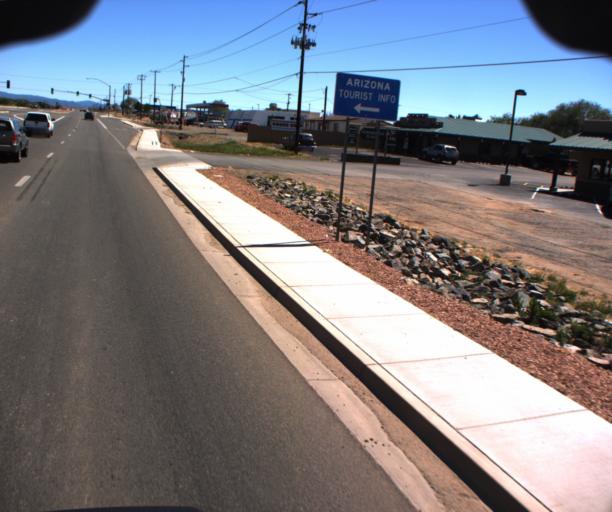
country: US
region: Arizona
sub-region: Yavapai County
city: Chino Valley
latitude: 34.7326
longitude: -112.4543
